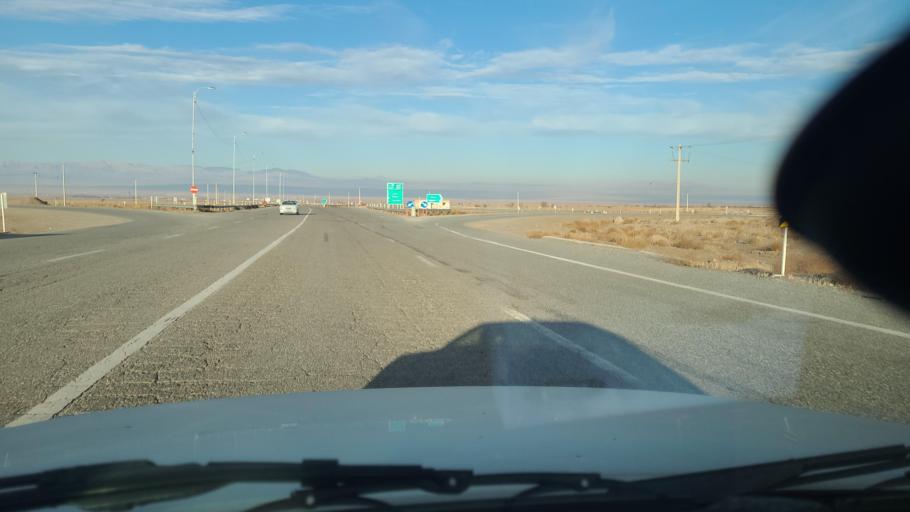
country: IR
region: Razavi Khorasan
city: Neqab
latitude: 36.5116
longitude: 57.5397
